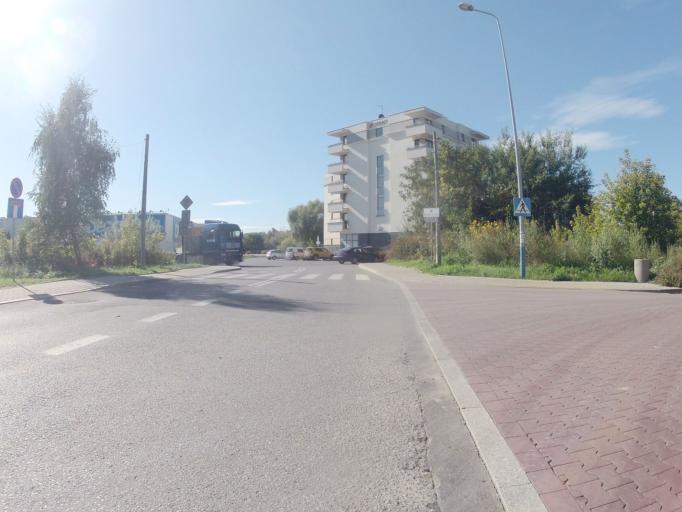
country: PL
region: Lesser Poland Voivodeship
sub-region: Krakow
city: Krakow
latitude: 50.0668
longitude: 19.9867
